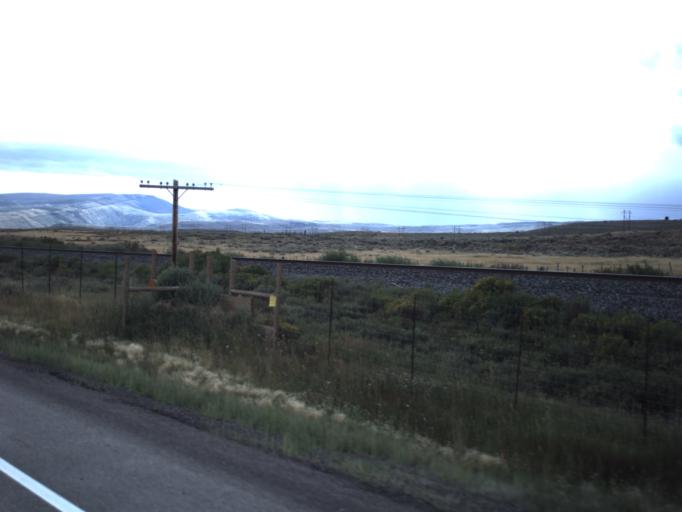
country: US
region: Utah
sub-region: Carbon County
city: Helper
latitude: 39.8833
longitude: -111.0472
